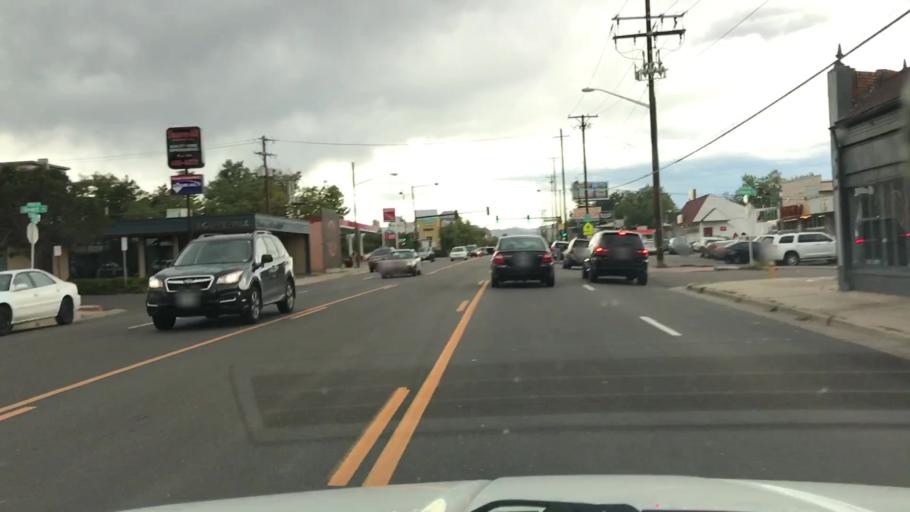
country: US
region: Colorado
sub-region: Jefferson County
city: Edgewater
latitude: 39.7694
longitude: -105.0424
